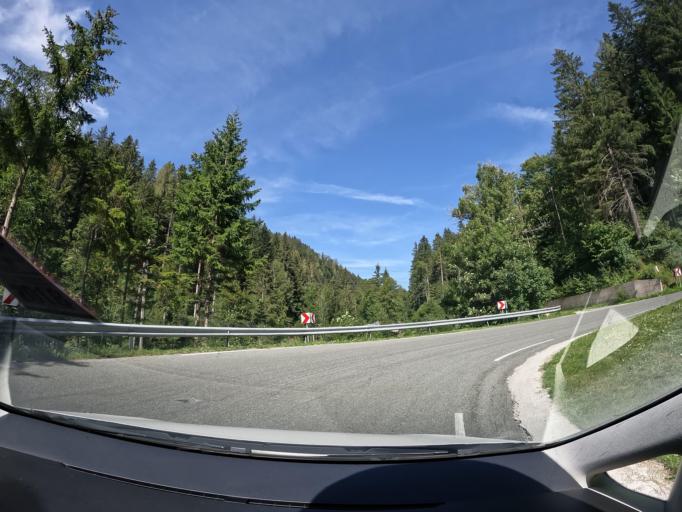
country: AT
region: Carinthia
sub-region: Politischer Bezirk Klagenfurt Land
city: Ludmannsdorf
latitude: 46.5041
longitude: 14.1003
